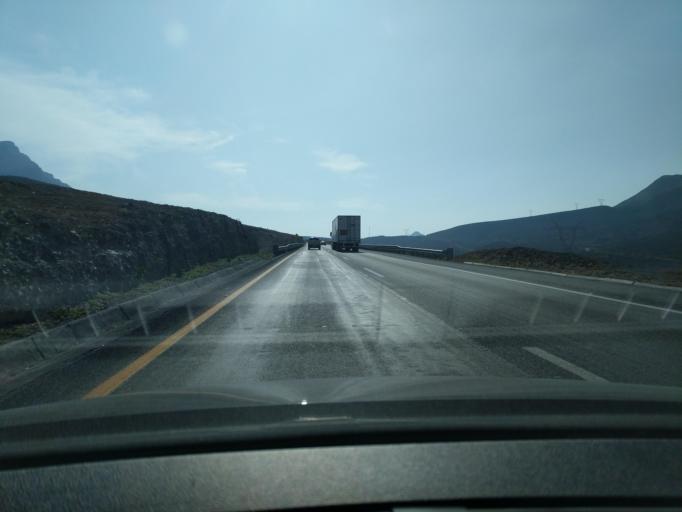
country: MX
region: Nuevo Leon
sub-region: Garcia
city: Las Torres de Guadalupe
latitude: 25.6538
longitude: -100.7234
